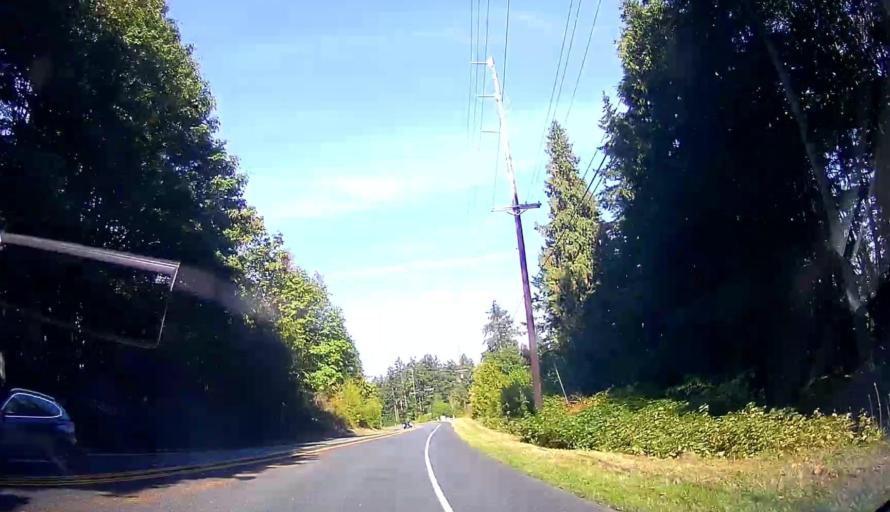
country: US
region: Washington
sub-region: Island County
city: Camano
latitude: 48.2040
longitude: -122.4826
